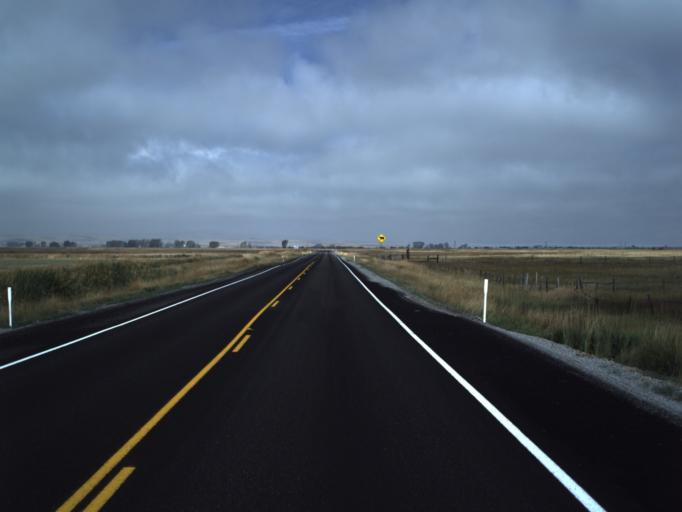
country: US
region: Utah
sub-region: Rich County
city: Randolph
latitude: 41.5035
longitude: -111.1244
